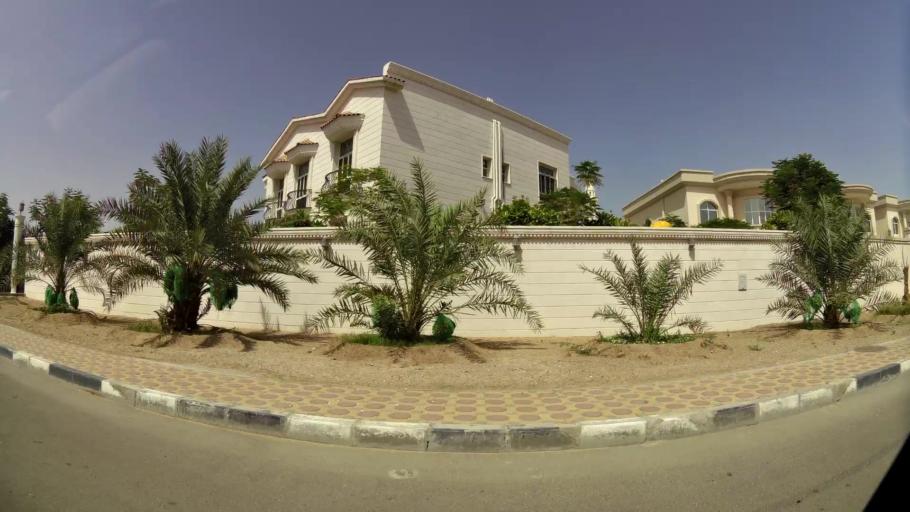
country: AE
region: Abu Dhabi
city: Al Ain
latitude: 24.2250
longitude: 55.6882
